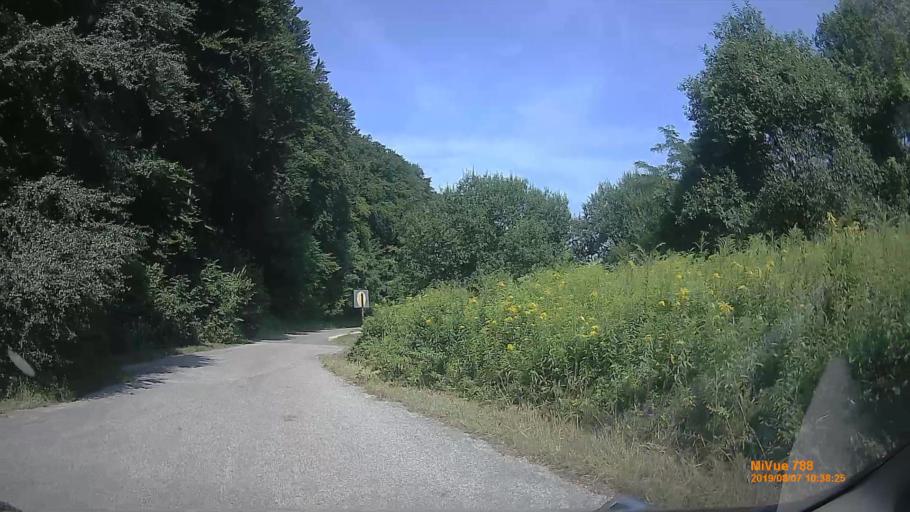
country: HU
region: Veszprem
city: Ajka
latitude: 47.0745
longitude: 17.5805
